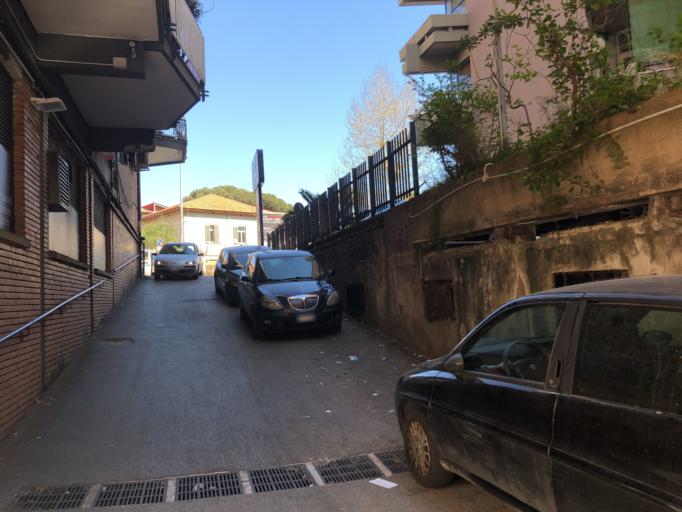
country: IT
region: Campania
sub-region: Provincia di Napoli
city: Napoli
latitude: 40.8605
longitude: 14.2214
